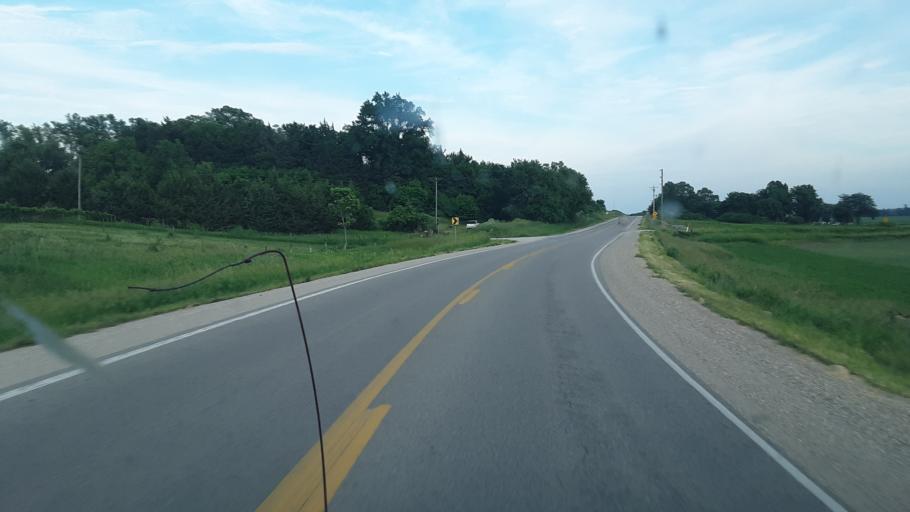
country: US
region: Iowa
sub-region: Benton County
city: Belle Plaine
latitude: 41.9193
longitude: -92.3574
